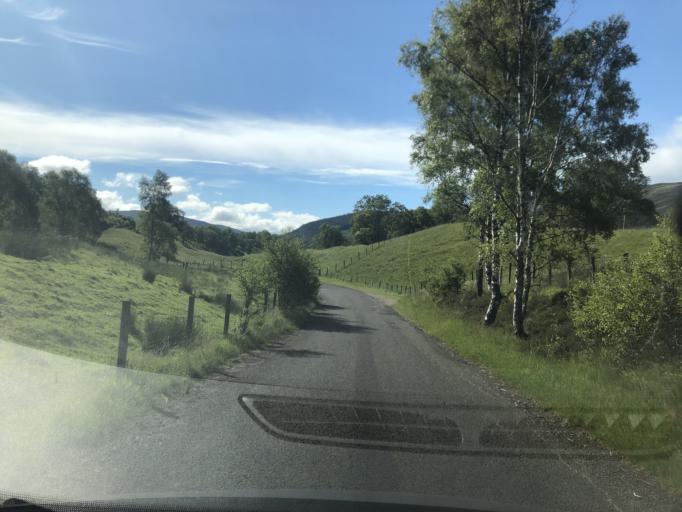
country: GB
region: Scotland
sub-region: Angus
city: Kirriemuir
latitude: 56.8393
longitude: -3.0901
